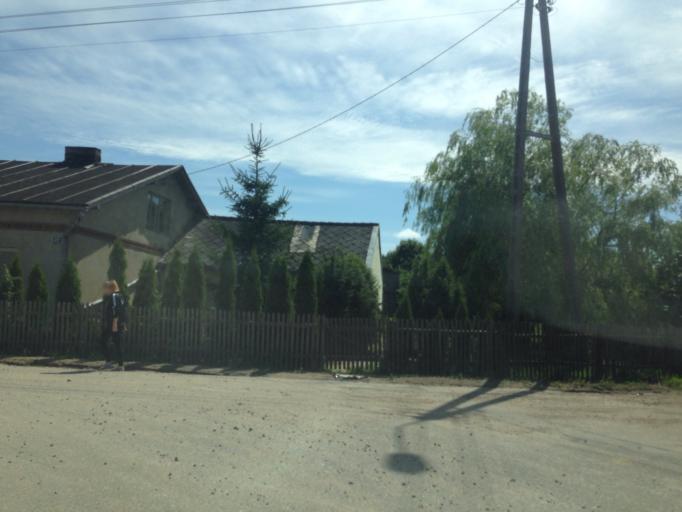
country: PL
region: Pomeranian Voivodeship
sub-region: Powiat koscierski
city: Karsin
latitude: 53.9489
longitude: 17.8712
